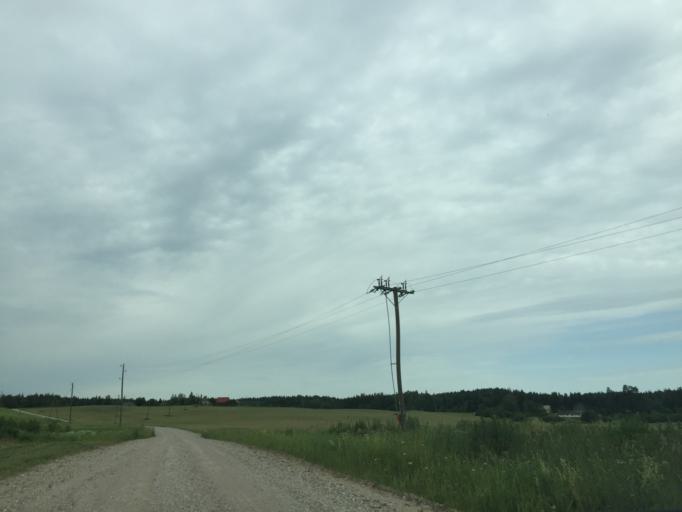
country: LV
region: Tukuma Rajons
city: Tukums
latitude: 57.0416
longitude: 23.1117
